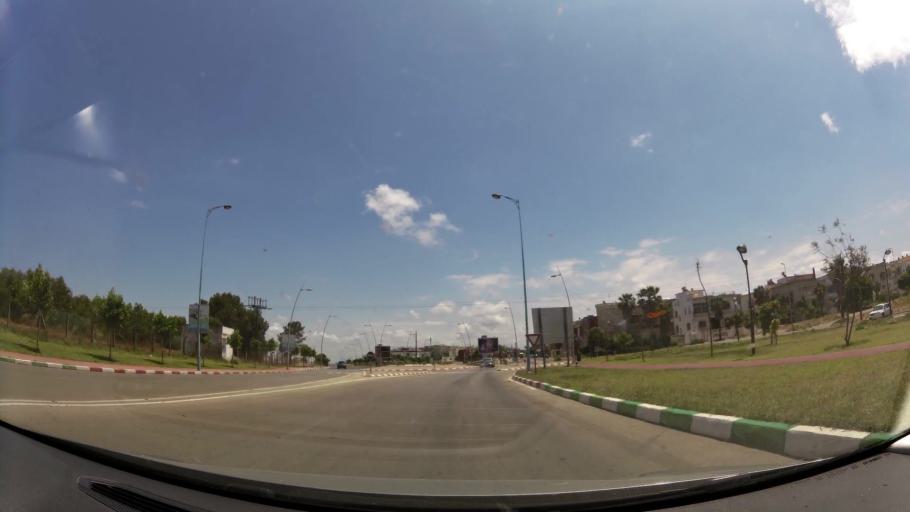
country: MA
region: Gharb-Chrarda-Beni Hssen
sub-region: Kenitra Province
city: Kenitra
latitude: 34.2751
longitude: -6.6151
